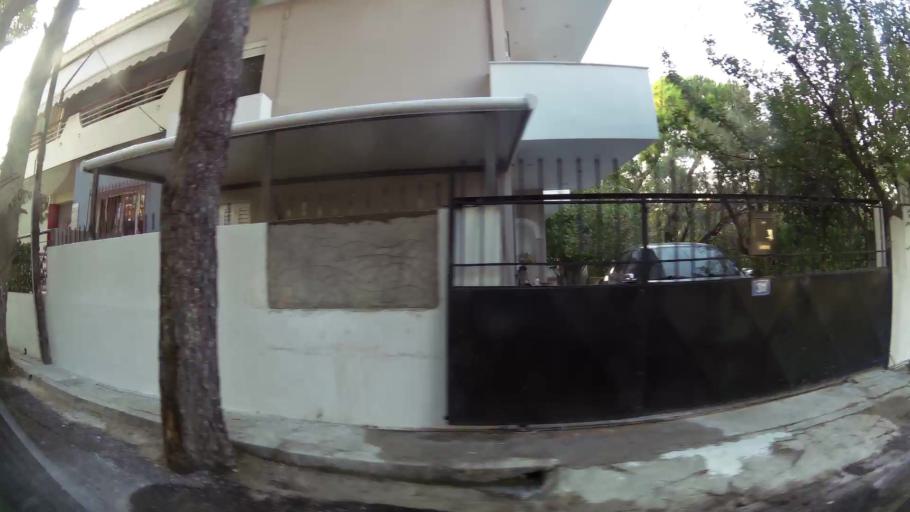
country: GR
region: Attica
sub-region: Nomarchia Athinas
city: Agia Paraskevi
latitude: 38.0169
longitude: 23.8399
